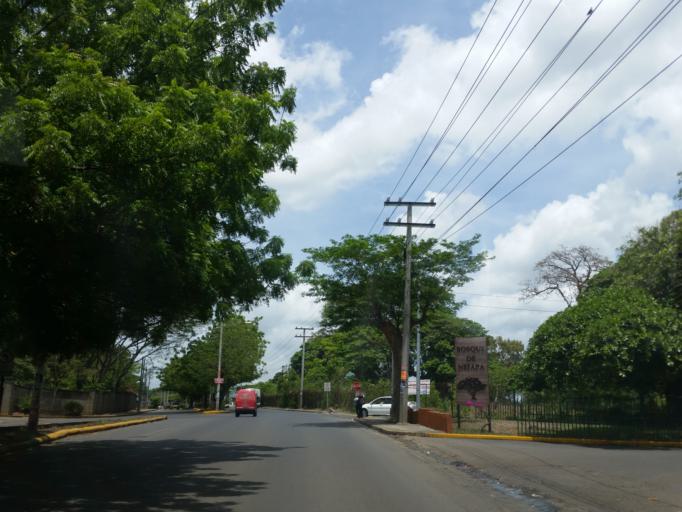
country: NI
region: Managua
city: Managua
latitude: 12.1152
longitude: -86.2863
